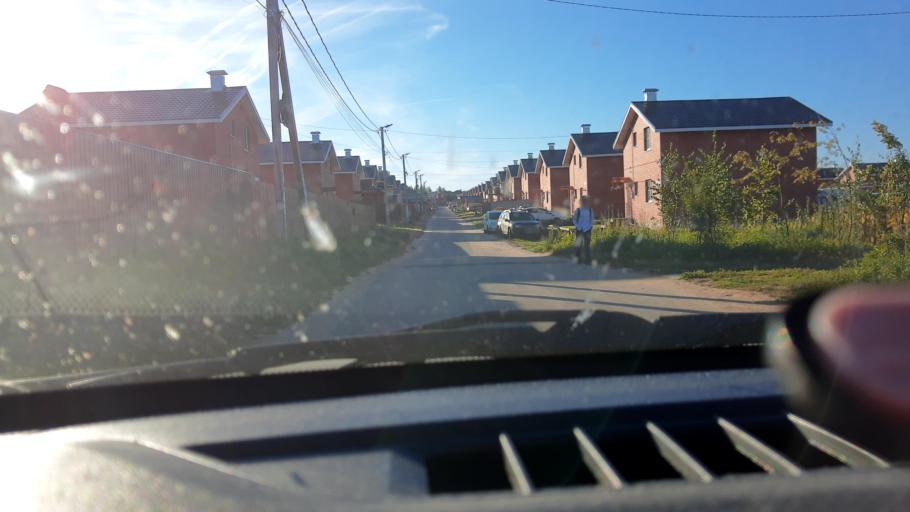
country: RU
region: Nizjnij Novgorod
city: Afonino
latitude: 56.2084
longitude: 44.1363
